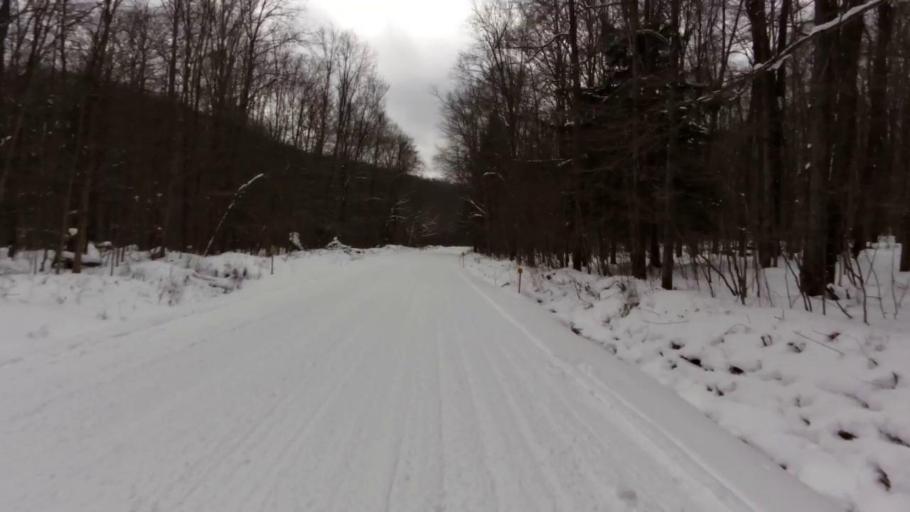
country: US
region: New York
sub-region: Cattaraugus County
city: Salamanca
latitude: 42.0243
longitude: -78.8152
